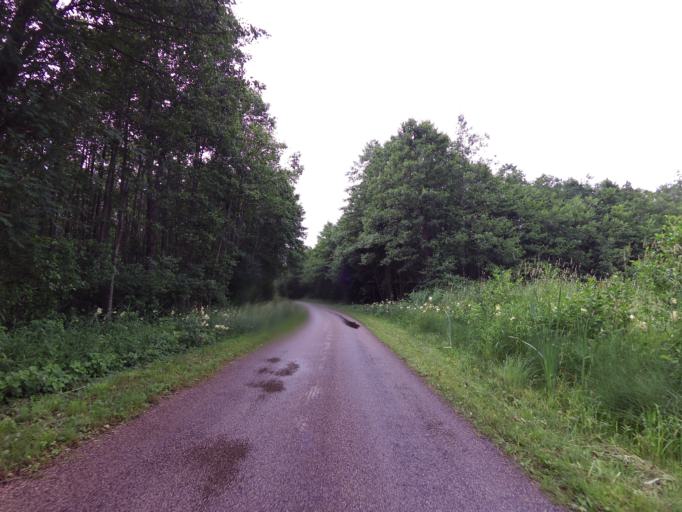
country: EE
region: Laeaene
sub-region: Vormsi vald
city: Hullo
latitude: 58.9943
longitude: 23.3266
